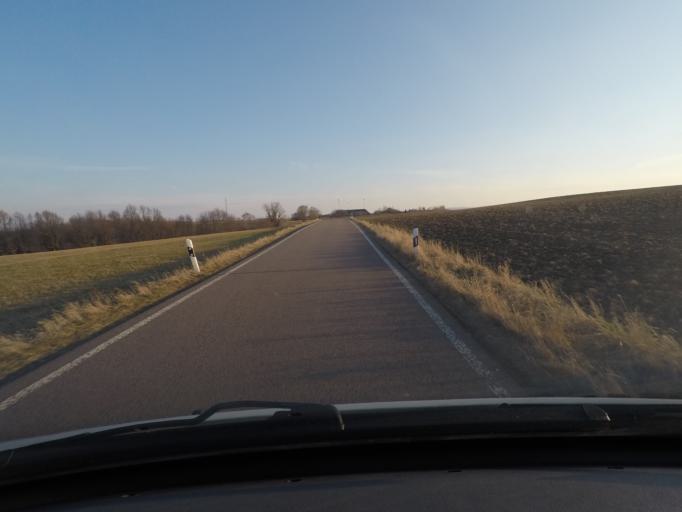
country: DE
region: Saxony
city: Reinhardtsgrimma
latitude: 50.9164
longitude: 13.7962
